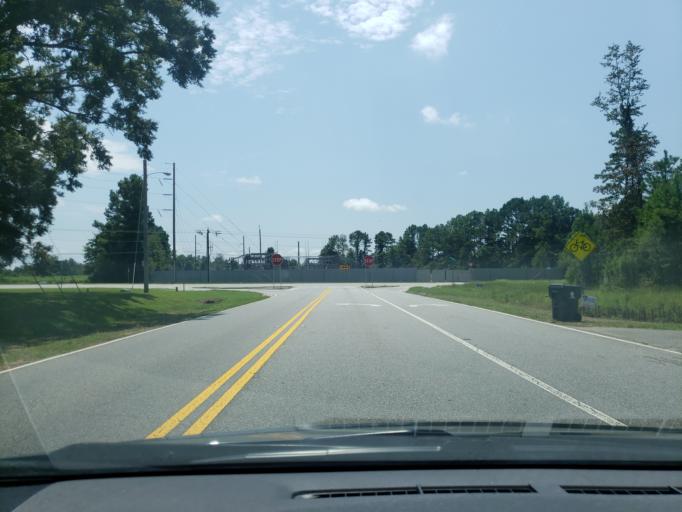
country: US
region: Georgia
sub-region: Dougherty County
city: Albany
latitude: 31.5864
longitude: -84.2813
